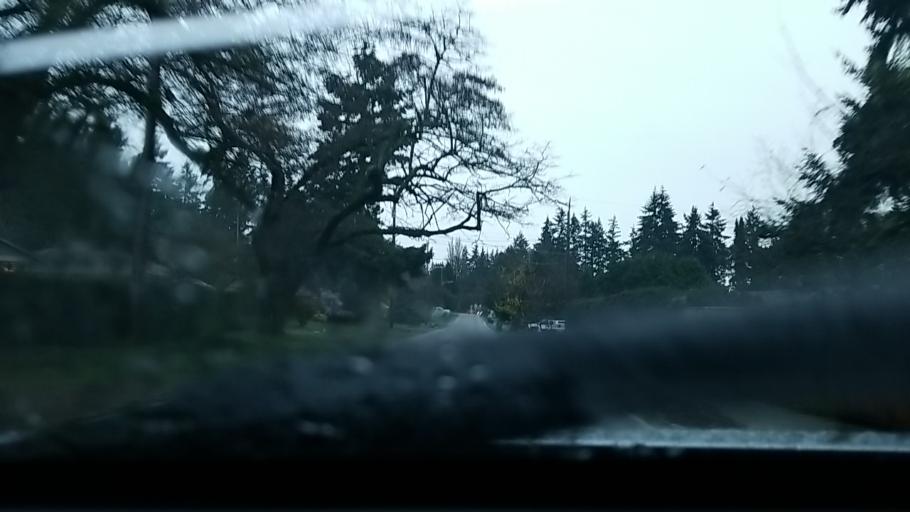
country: US
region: Washington
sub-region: King County
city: Shoreline
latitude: 47.7214
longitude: -122.3305
